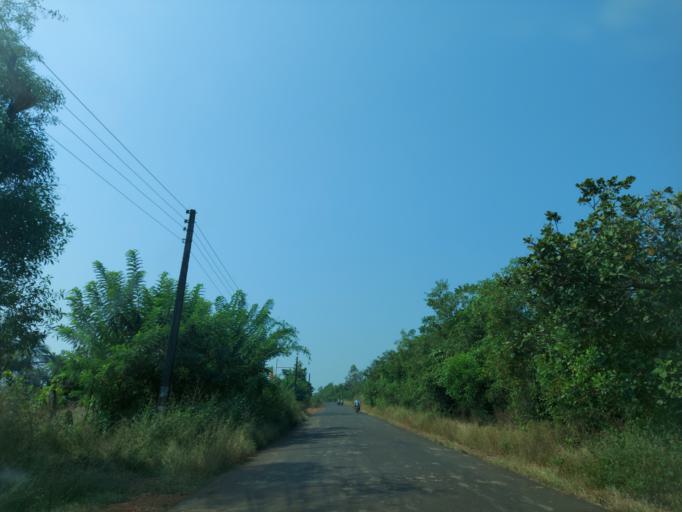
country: IN
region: Maharashtra
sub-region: Sindhudurg
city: Kudal
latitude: 15.9780
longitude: 73.6548
